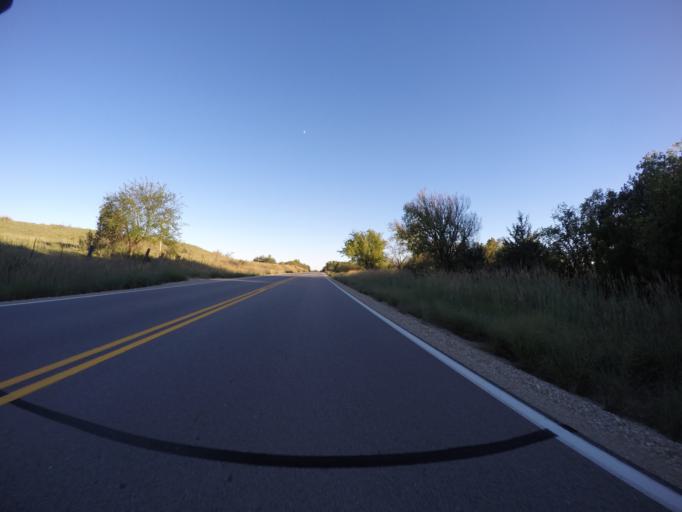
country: US
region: Kansas
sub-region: Riley County
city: Fort Riley North
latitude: 39.2508
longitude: -96.7705
